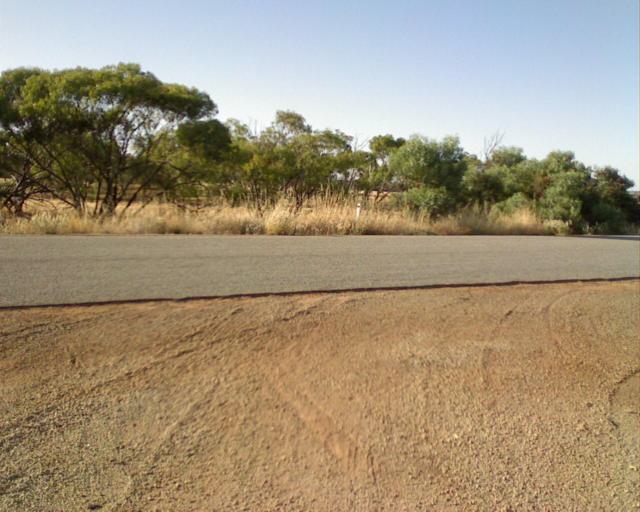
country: AU
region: Western Australia
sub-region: Merredin
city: Merredin
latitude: -31.0591
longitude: 117.8028
